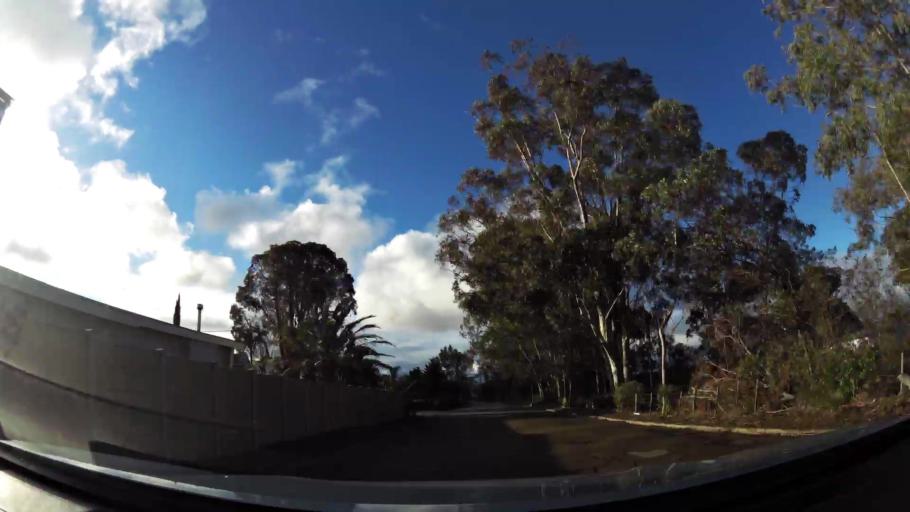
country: ZA
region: Western Cape
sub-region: Eden District Municipality
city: Riversdale
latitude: -34.2083
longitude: 21.5886
